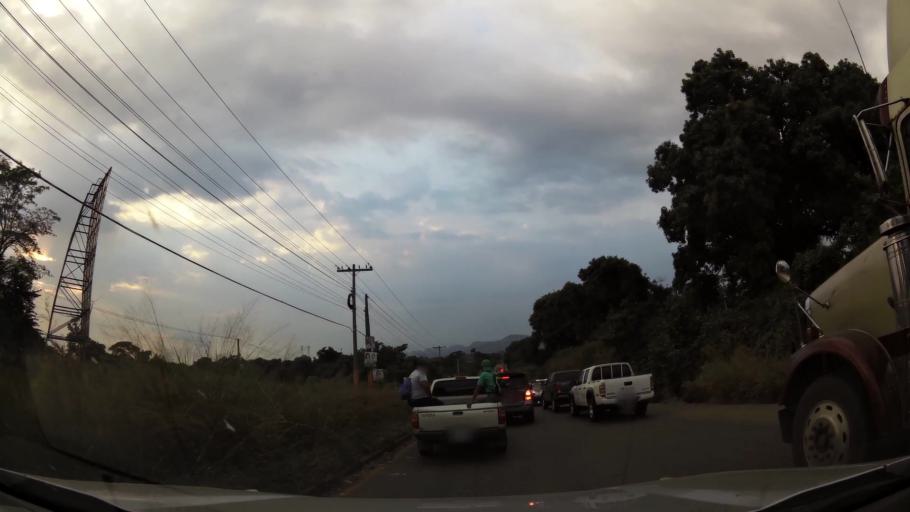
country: GT
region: Escuintla
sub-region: Municipio de Escuintla
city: Escuintla
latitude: 14.2839
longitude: -90.7898
